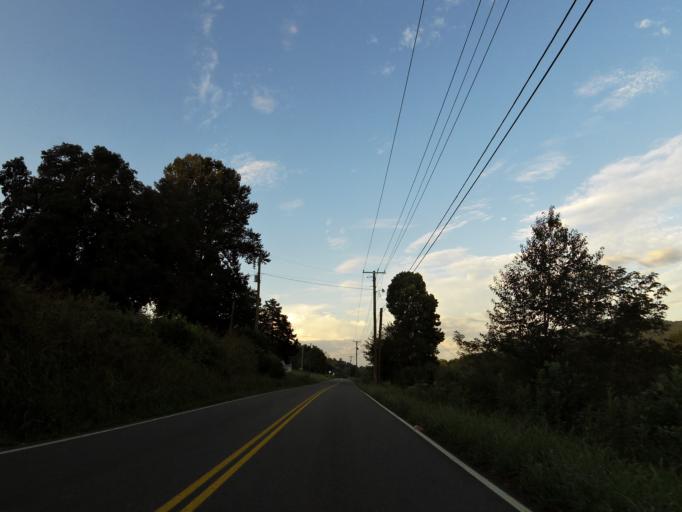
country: US
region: Tennessee
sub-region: Union County
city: Luttrell
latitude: 36.2495
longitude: -83.6758
